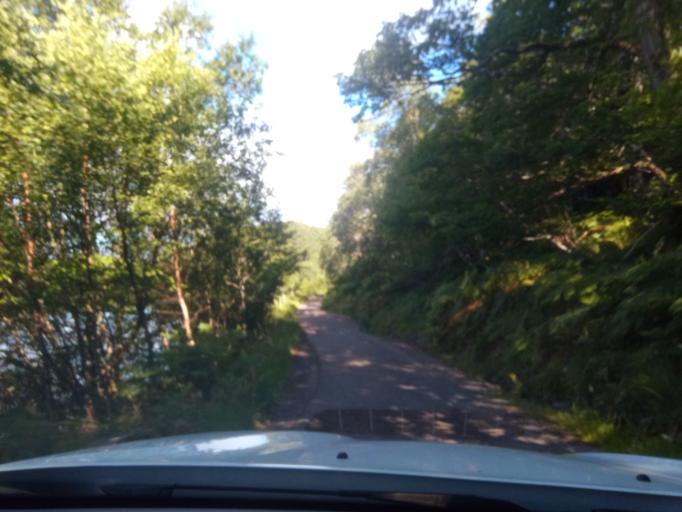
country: GB
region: Scotland
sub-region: Argyll and Bute
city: Isle Of Mull
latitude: 56.7633
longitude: -5.8195
